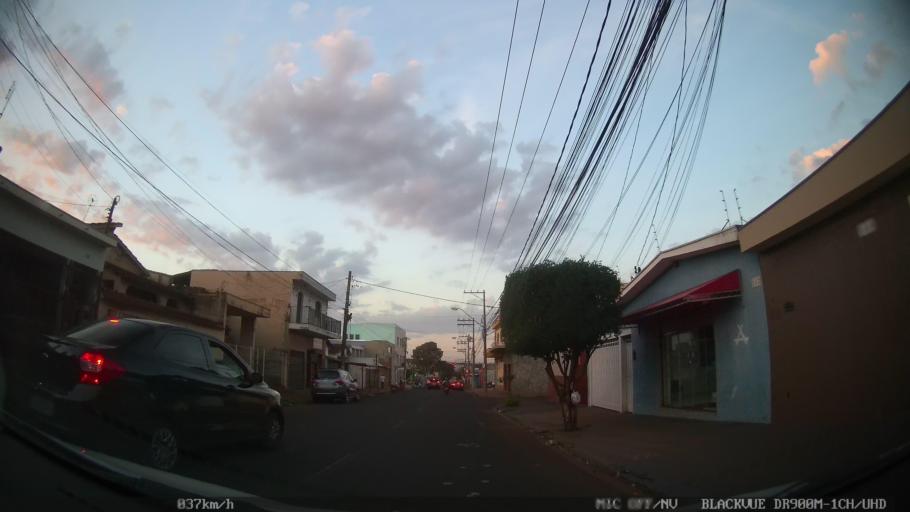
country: BR
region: Sao Paulo
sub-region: Ribeirao Preto
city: Ribeirao Preto
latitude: -21.1526
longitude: -47.8254
